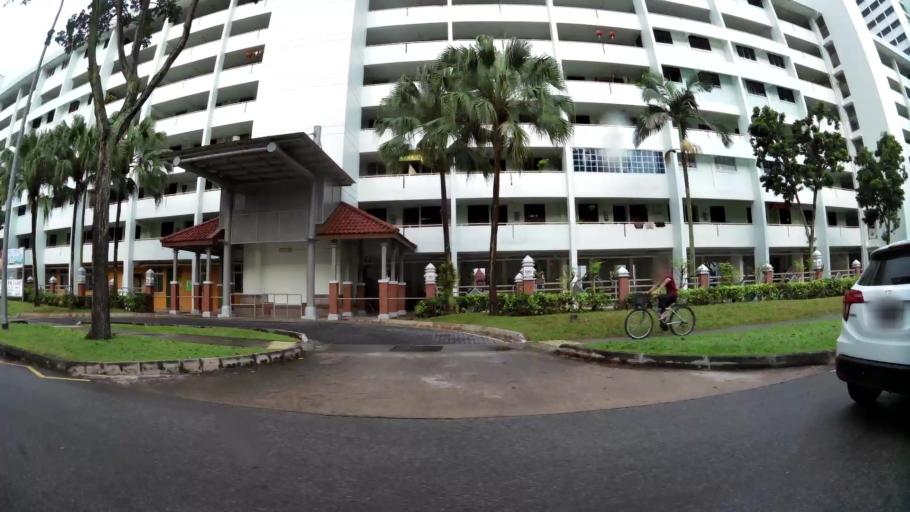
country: SG
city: Singapore
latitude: 1.3737
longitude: 103.8557
